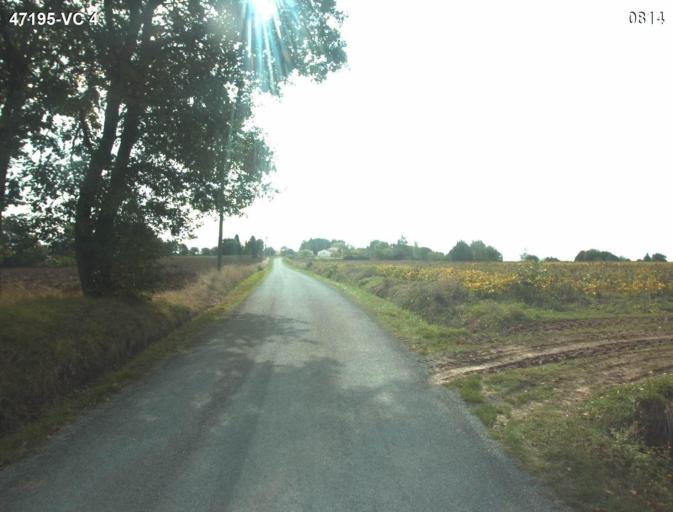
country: FR
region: Aquitaine
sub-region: Departement du Lot-et-Garonne
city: Nerac
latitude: 44.1143
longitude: 0.3803
